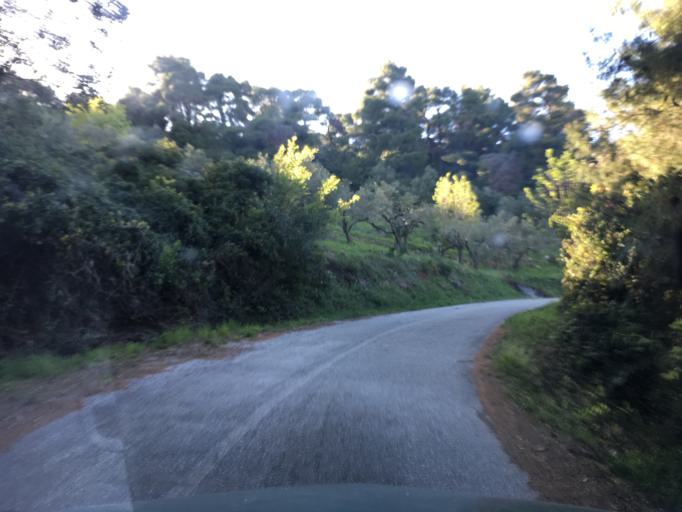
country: GR
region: Thessaly
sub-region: Nomos Magnisias
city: Skopelos
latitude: 39.1841
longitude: 23.6190
